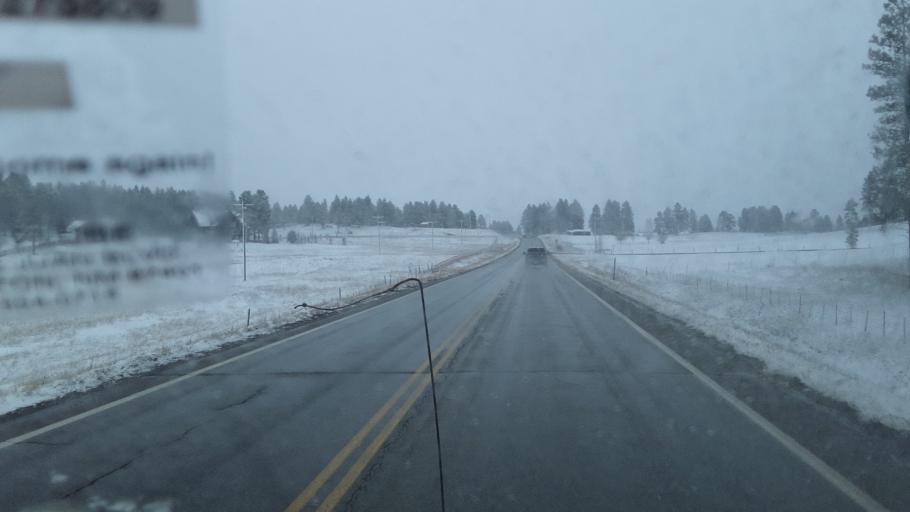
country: US
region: Colorado
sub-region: Archuleta County
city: Pagosa Springs
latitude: 37.2285
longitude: -106.9854
